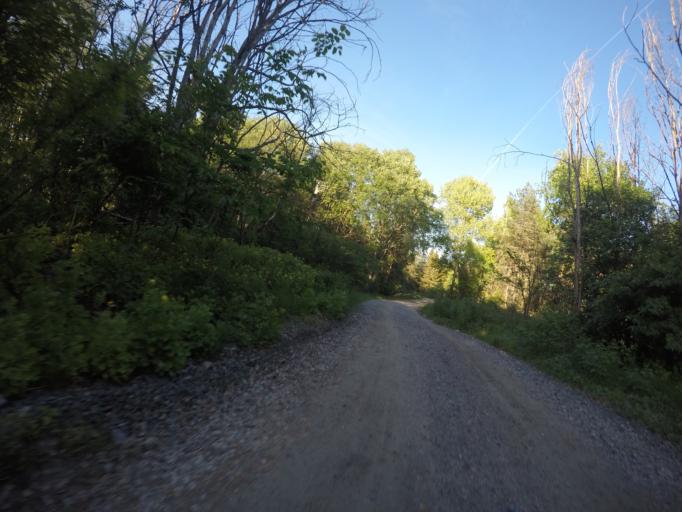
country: SE
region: Soedermanland
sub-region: Eskilstuna Kommun
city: Eskilstuna
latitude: 59.3500
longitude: 16.5332
